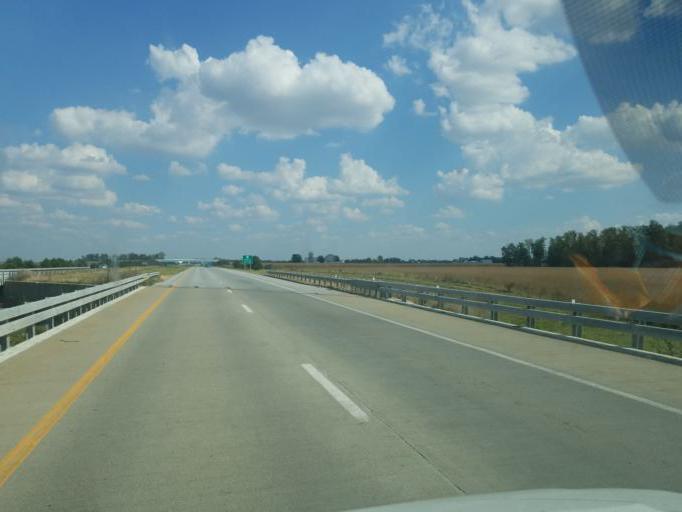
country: US
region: Ohio
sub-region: Allen County
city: Delphos
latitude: 40.8733
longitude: -84.3745
